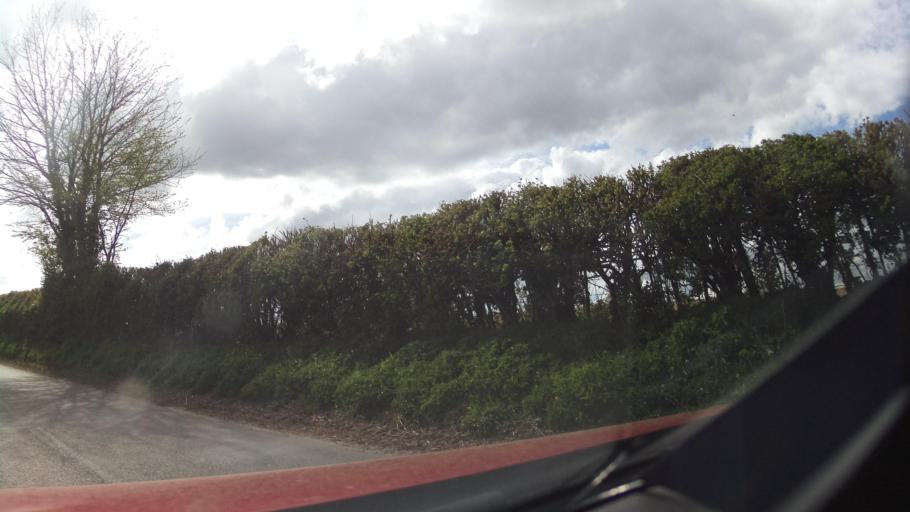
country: GB
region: England
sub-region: Hampshire
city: Abbotts Ann
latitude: 51.0990
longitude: -1.5107
